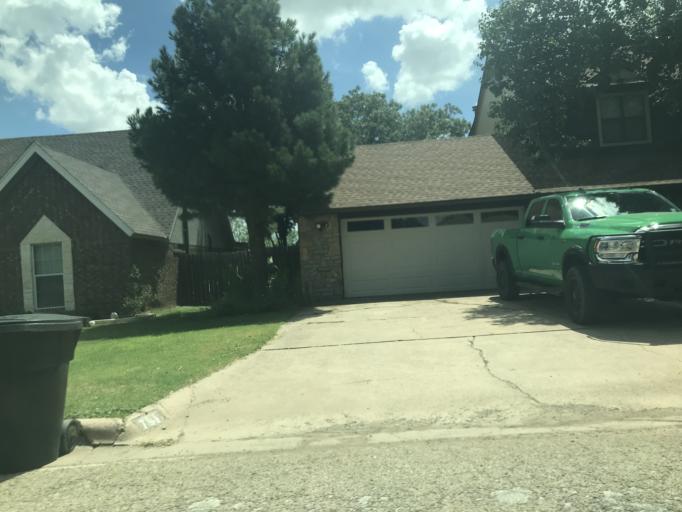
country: US
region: Texas
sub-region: Taylor County
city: Abilene
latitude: 32.4428
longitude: -99.6978
